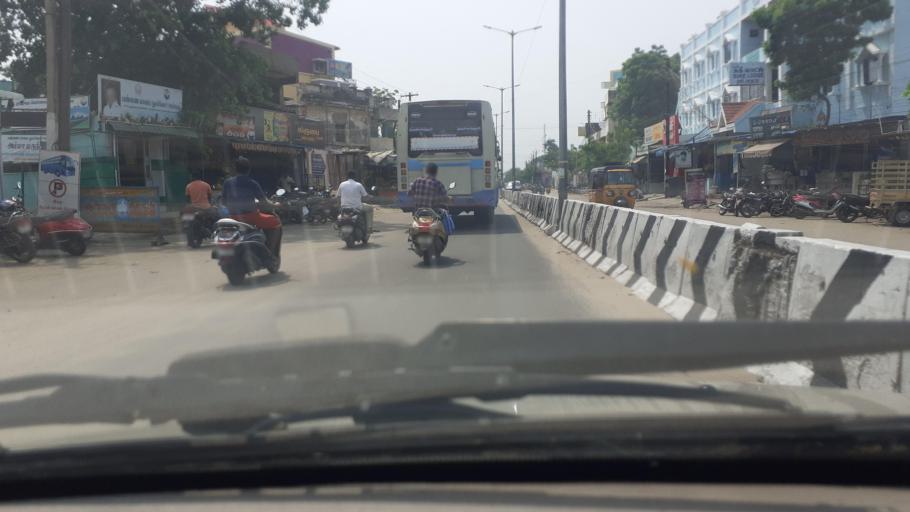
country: IN
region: Tamil Nadu
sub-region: Thoothukkudi
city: Korampallam
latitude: 8.8119
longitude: 78.1373
